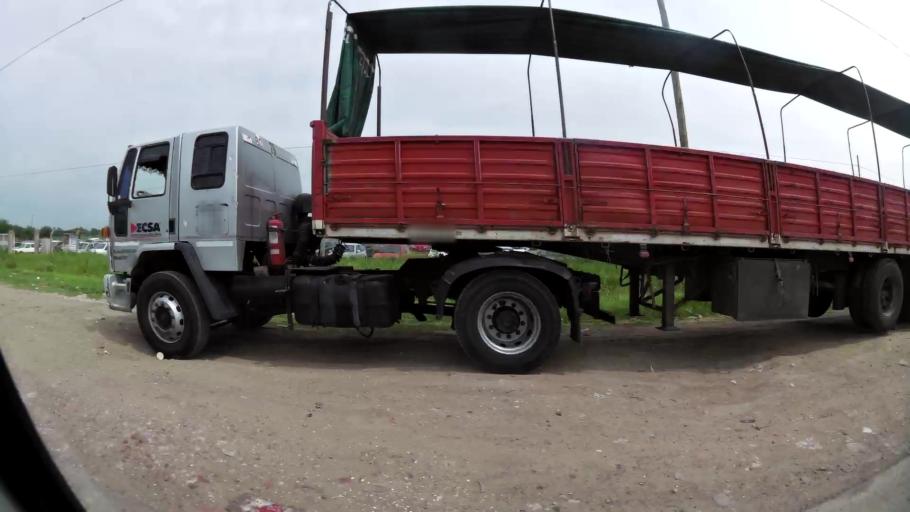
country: AR
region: Buenos Aires
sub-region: Partido de La Plata
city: La Plata
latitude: -34.9059
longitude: -57.9997
